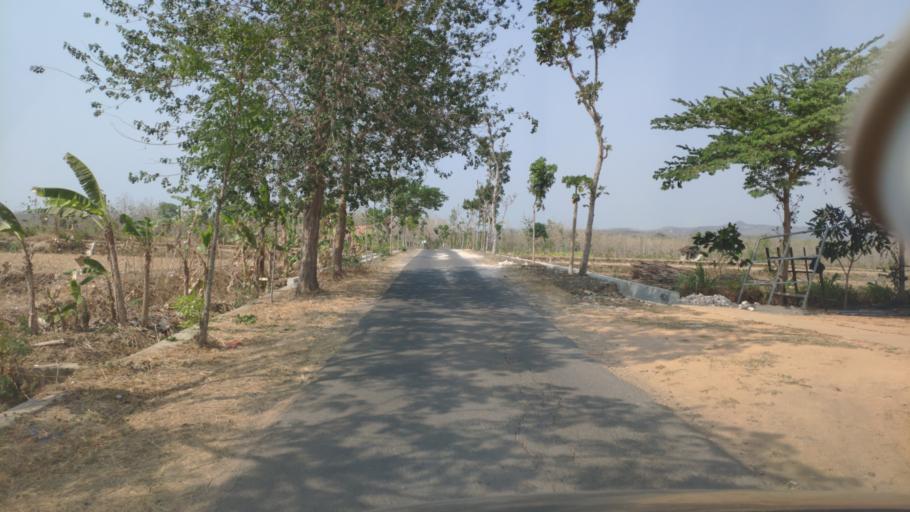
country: ID
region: Central Java
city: Karanggeneng
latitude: -6.9198
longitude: 111.4521
